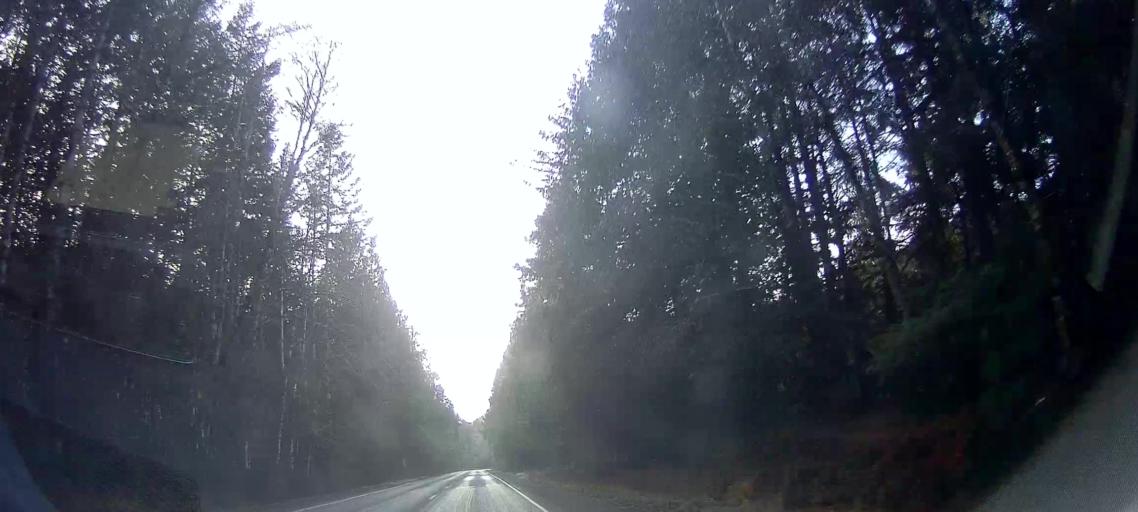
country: US
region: Washington
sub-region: Snohomish County
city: Darrington
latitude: 48.5614
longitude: -121.8239
